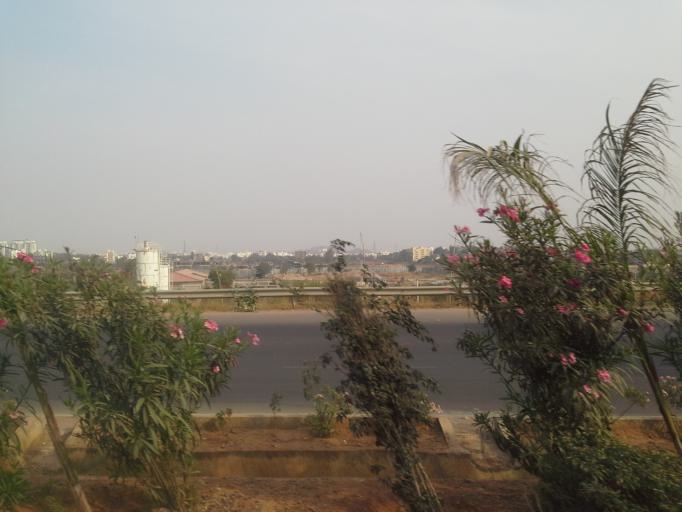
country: IN
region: Telangana
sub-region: Rangareddi
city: Kukatpalli
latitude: 17.3998
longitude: 78.3523
